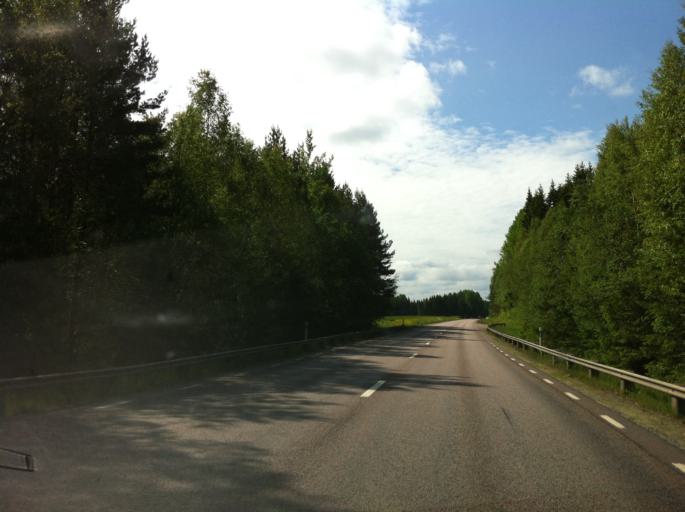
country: SE
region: Vaermland
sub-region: Karlstads Kommun
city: Edsvalla
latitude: 59.4564
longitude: 13.2110
